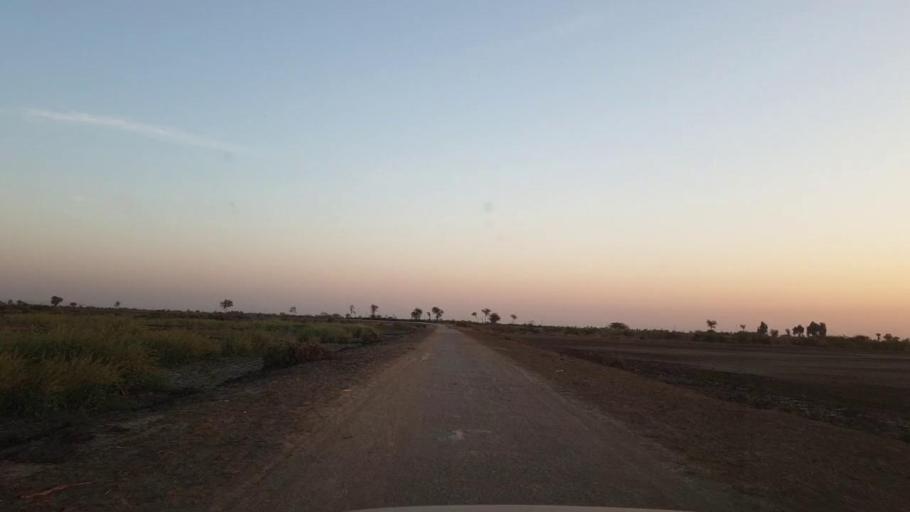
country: PK
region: Sindh
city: Samaro
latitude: 25.1506
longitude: 69.4258
